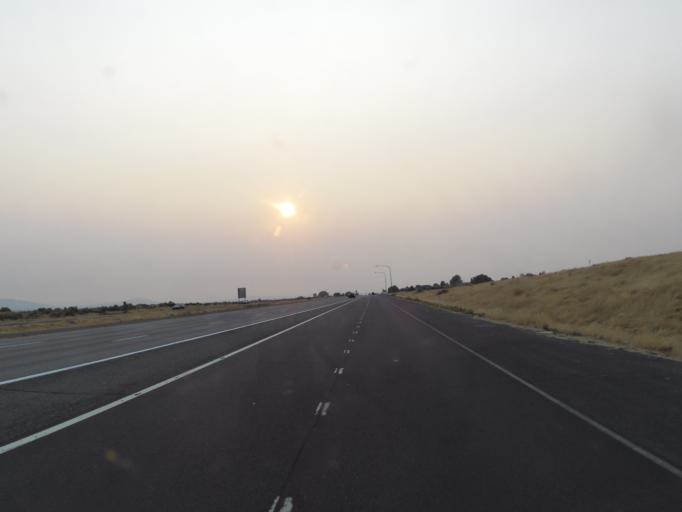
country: US
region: Washington
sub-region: Franklin County
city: West Pasco
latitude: 46.2682
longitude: -119.1897
